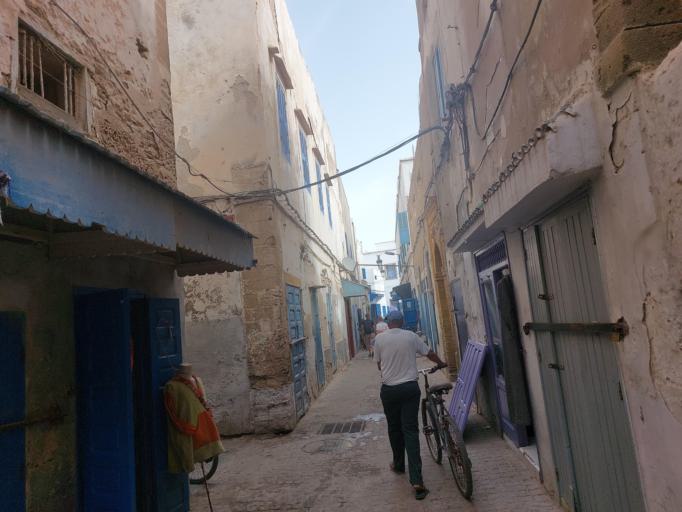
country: MA
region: Marrakech-Tensift-Al Haouz
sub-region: Essaouira
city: Essaouira
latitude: 31.5128
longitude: -9.7679
